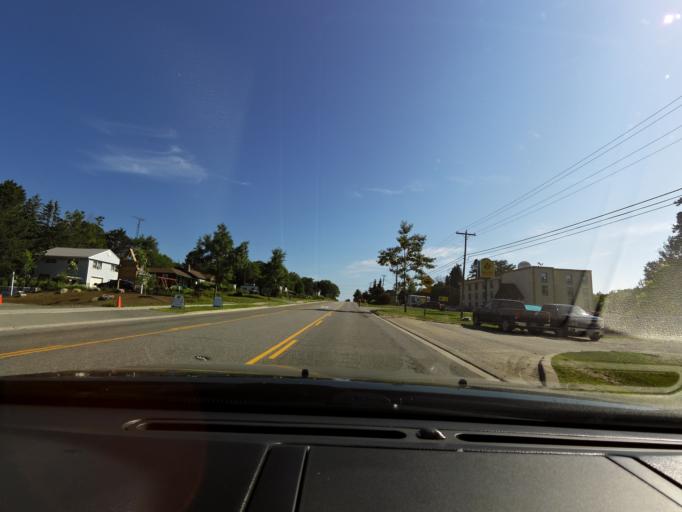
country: CA
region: Ontario
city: Huntsville
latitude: 45.3138
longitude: -79.2418
